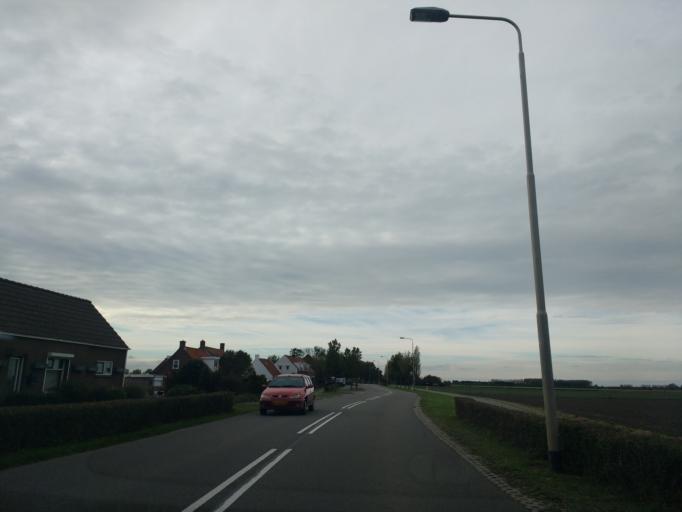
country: NL
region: Zeeland
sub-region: Gemeente Vlissingen
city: Vlissingen
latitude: 51.3836
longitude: 3.5445
